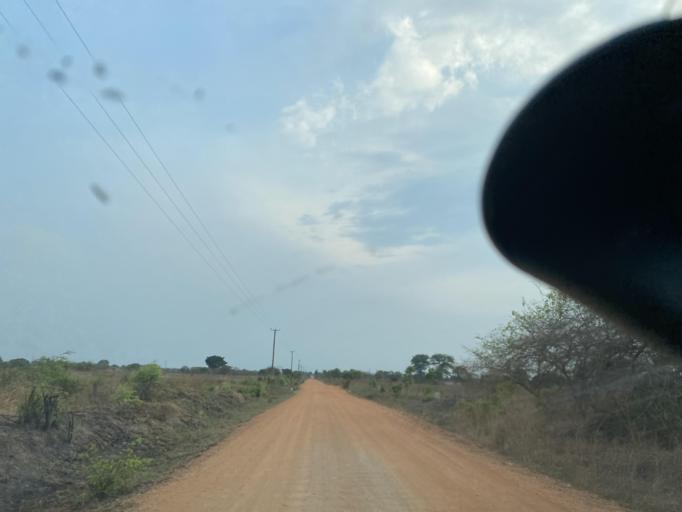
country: ZM
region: Lusaka
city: Chongwe
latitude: -15.2067
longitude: 28.5806
